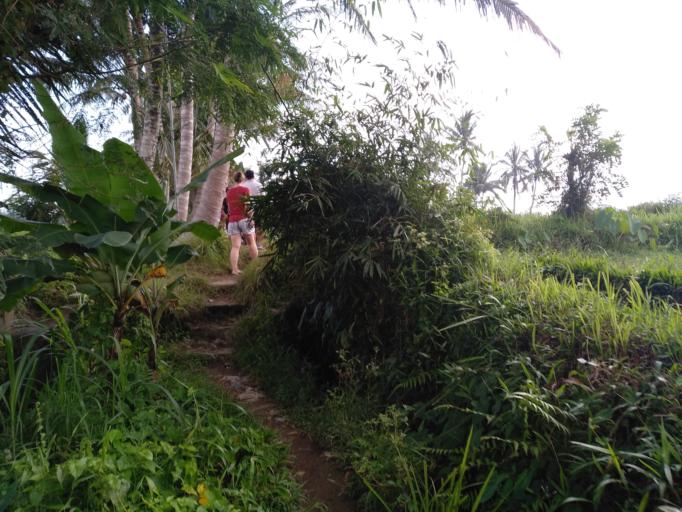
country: ID
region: Bali
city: Banjar Pande
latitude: -8.4960
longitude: 115.2474
